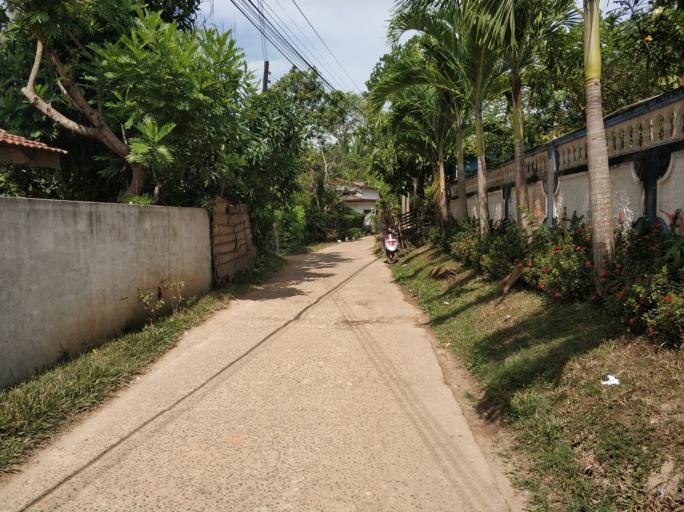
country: LK
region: Southern
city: Weligama
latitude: 5.9633
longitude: 80.4030
